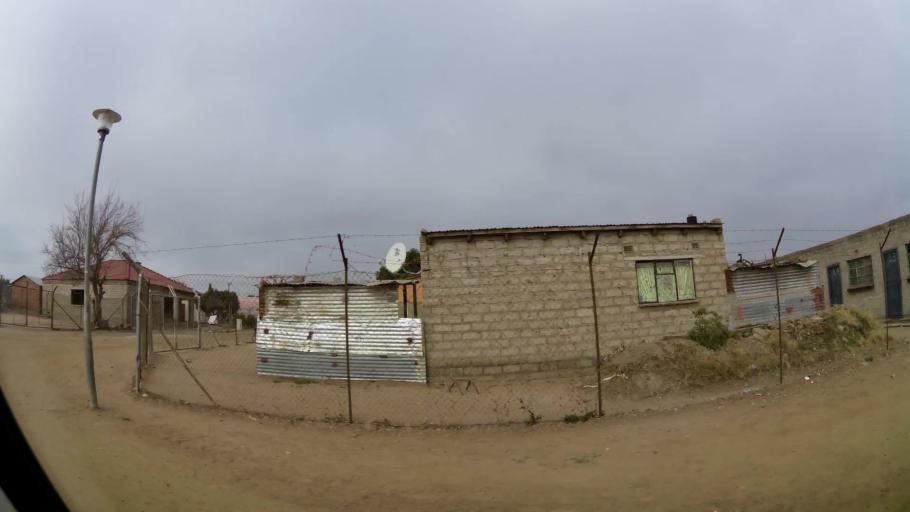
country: ZA
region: Limpopo
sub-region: Capricorn District Municipality
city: Polokwane
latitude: -23.8386
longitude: 29.3827
